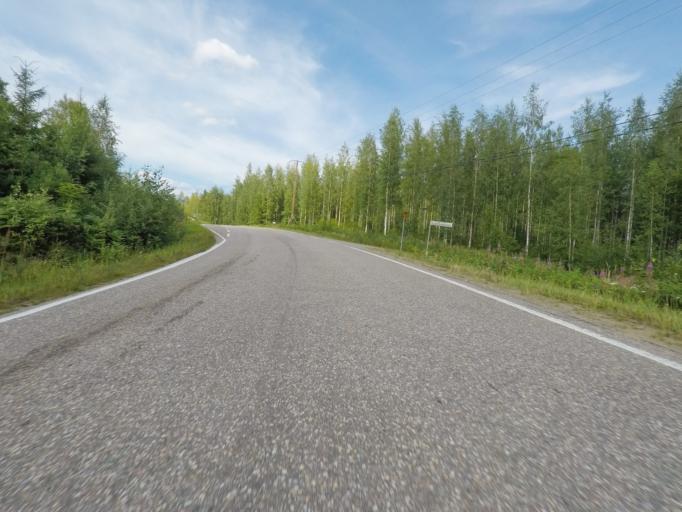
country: FI
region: Southern Savonia
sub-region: Savonlinna
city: Sulkava
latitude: 61.7554
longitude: 28.2269
